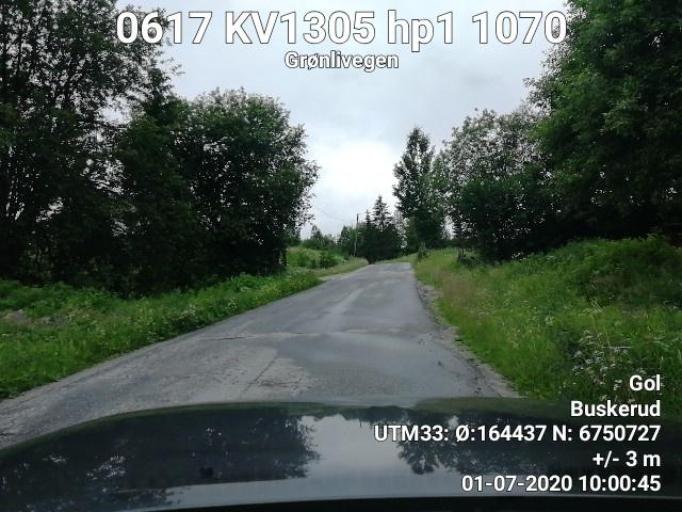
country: NO
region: Buskerud
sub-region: Gol
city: Gol
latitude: 60.7502
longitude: 8.8378
